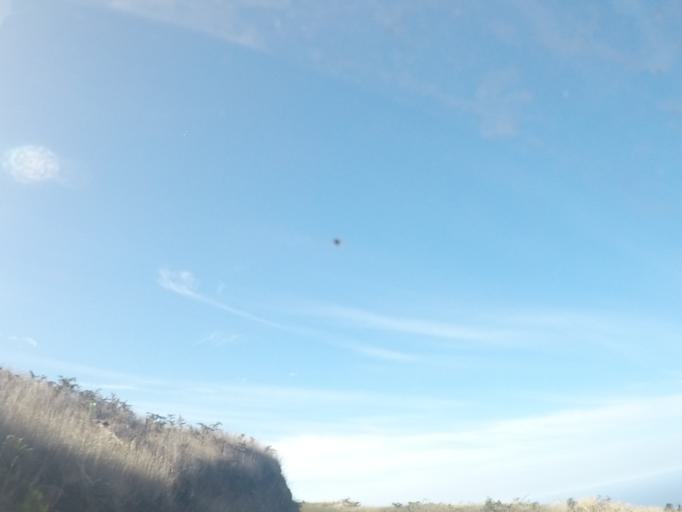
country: PT
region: Madeira
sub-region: Funchal
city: Nossa Senhora do Monte
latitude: 32.7065
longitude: -16.8995
